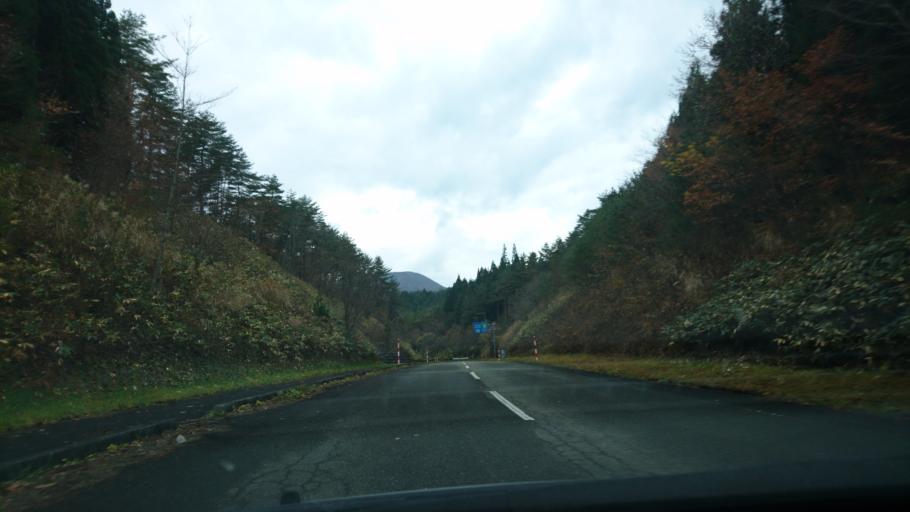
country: JP
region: Iwate
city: Ichinoseki
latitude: 38.9233
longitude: 140.9131
